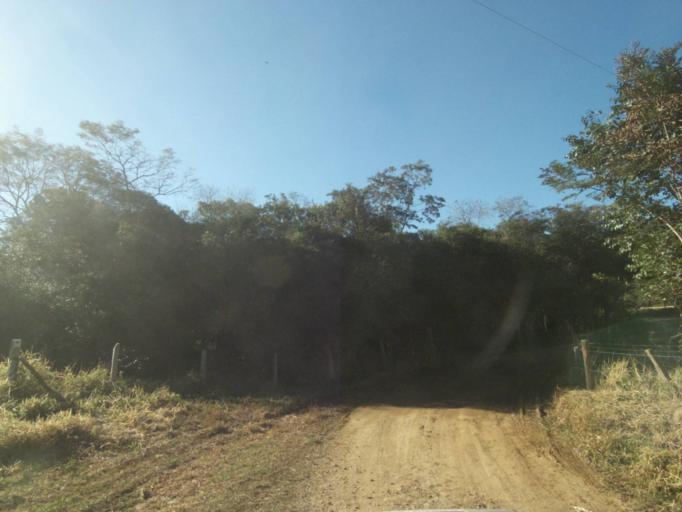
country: BR
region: Parana
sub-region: Tibagi
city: Tibagi
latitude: -24.5567
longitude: -50.5196
